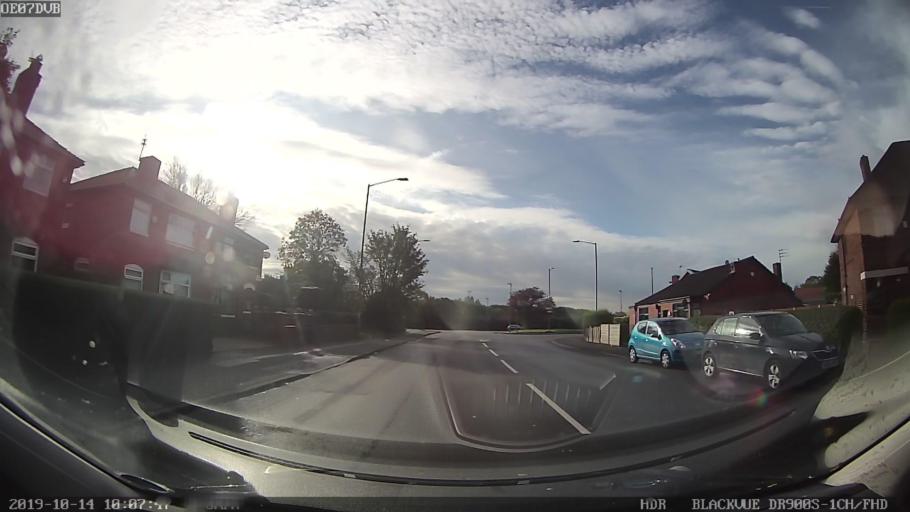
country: GB
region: England
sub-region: Manchester
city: Failsworth
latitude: 53.5203
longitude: -2.1818
